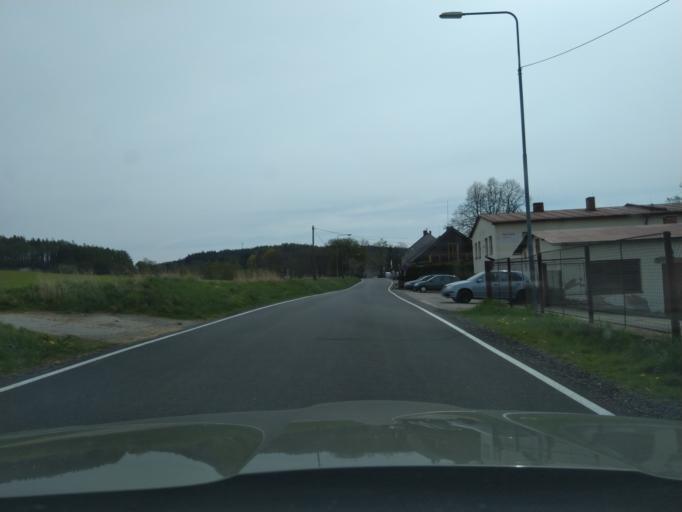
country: CZ
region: Jihocesky
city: Vacov
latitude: 49.1347
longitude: 13.7331
